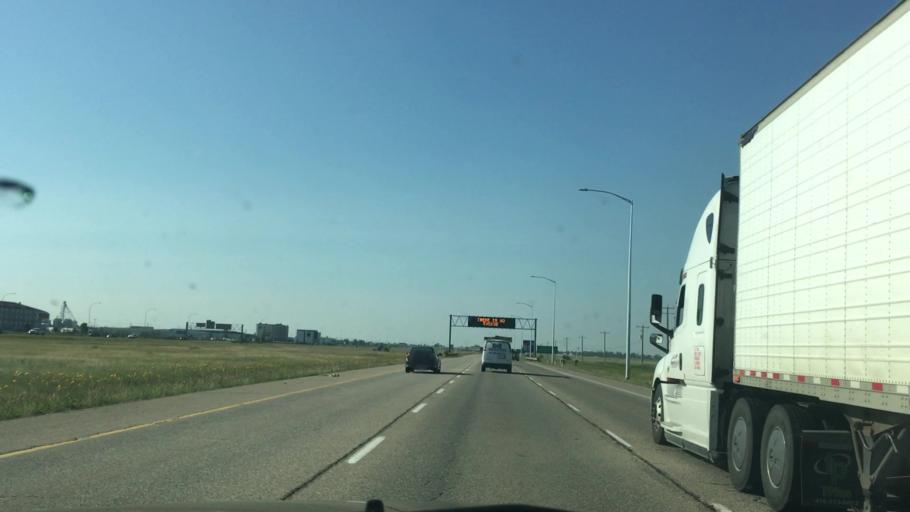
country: CA
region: Alberta
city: Leduc
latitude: 53.3015
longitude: -113.5500
